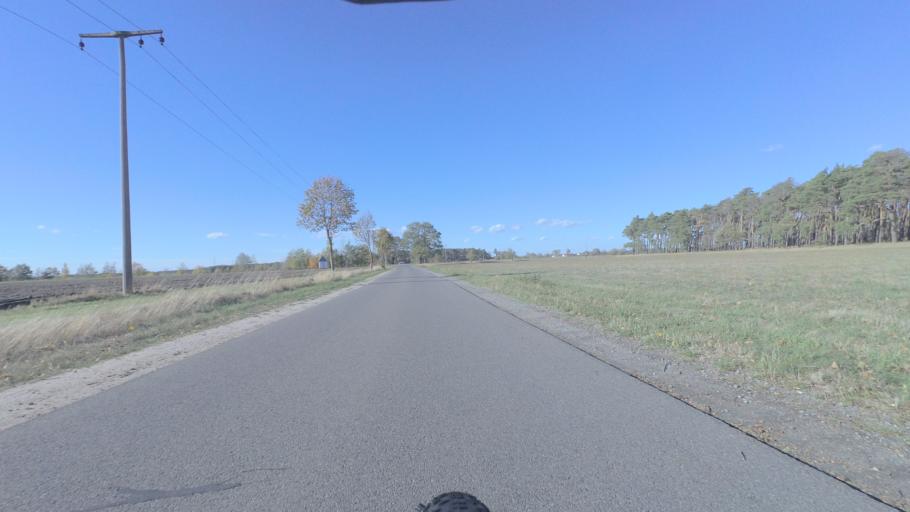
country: DE
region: Saxony
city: Nauwalde
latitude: 51.4421
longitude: 13.4316
